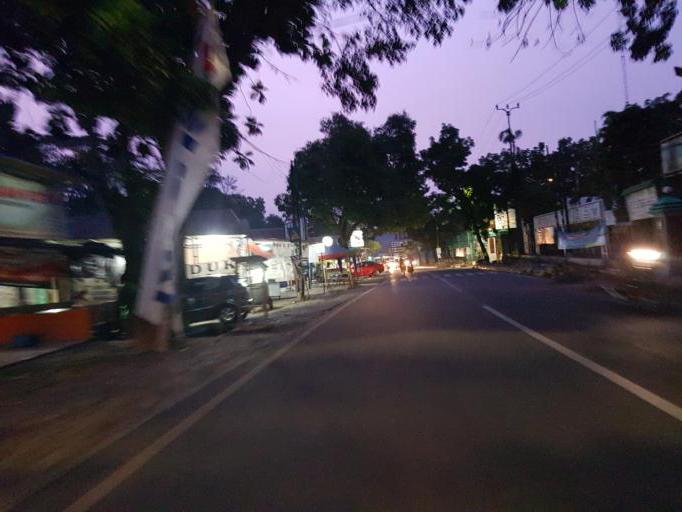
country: ID
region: West Java
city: Serpong
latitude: -6.3150
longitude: 106.6616
